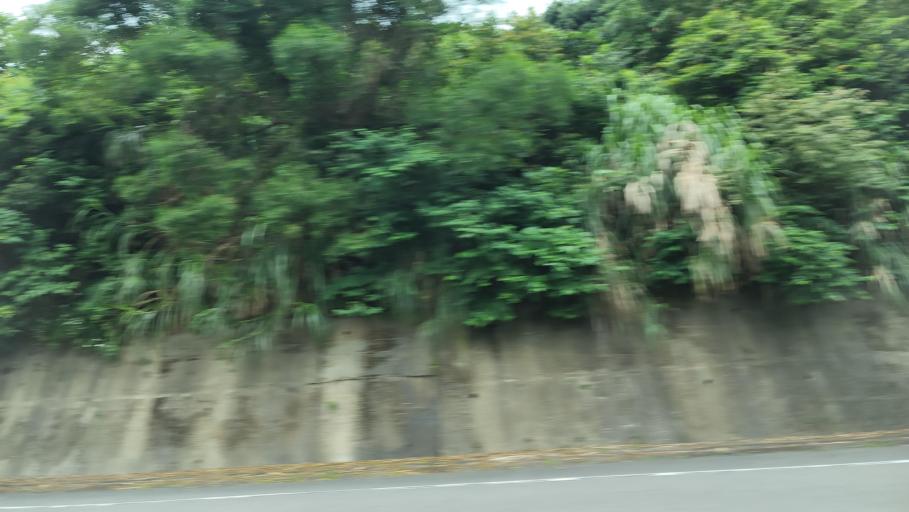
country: TW
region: Taiwan
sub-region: Keelung
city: Keelung
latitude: 25.1966
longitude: 121.6830
